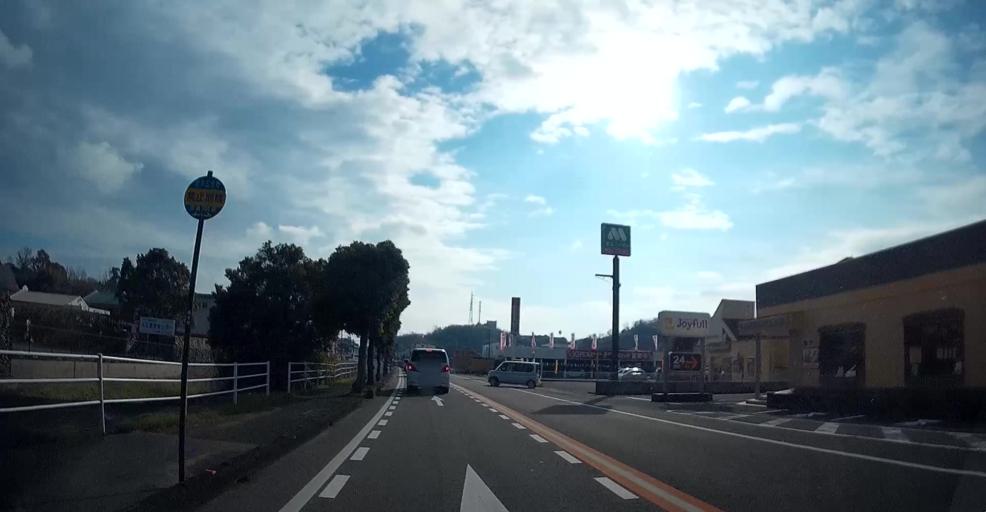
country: JP
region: Kumamoto
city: Yatsushiro
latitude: 32.5916
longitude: 130.4301
